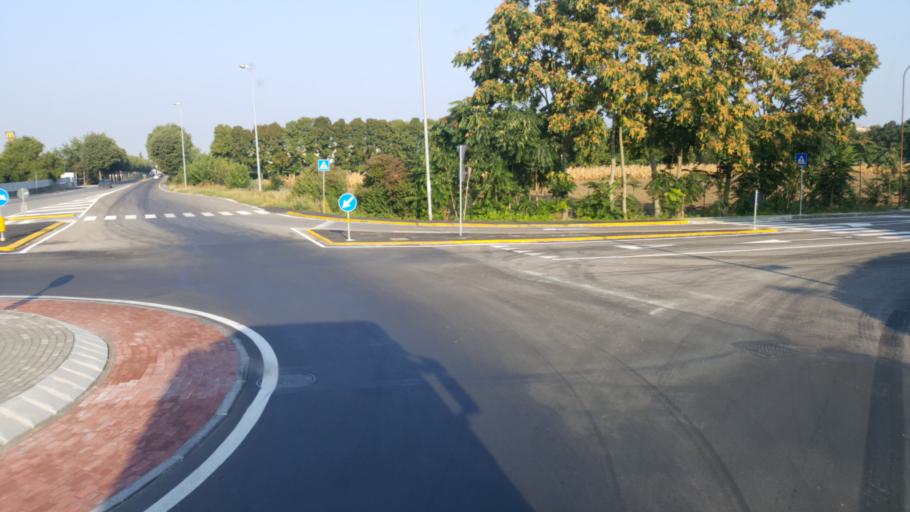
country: IT
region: Lombardy
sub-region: Provincia di Pavia
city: Voghera
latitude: 44.9864
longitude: 9.0031
